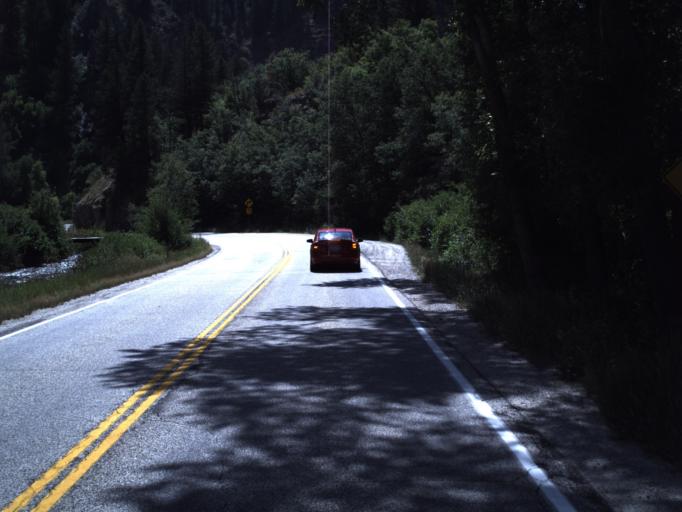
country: US
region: Utah
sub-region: Cache County
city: North Logan
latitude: 41.8158
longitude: -111.6182
